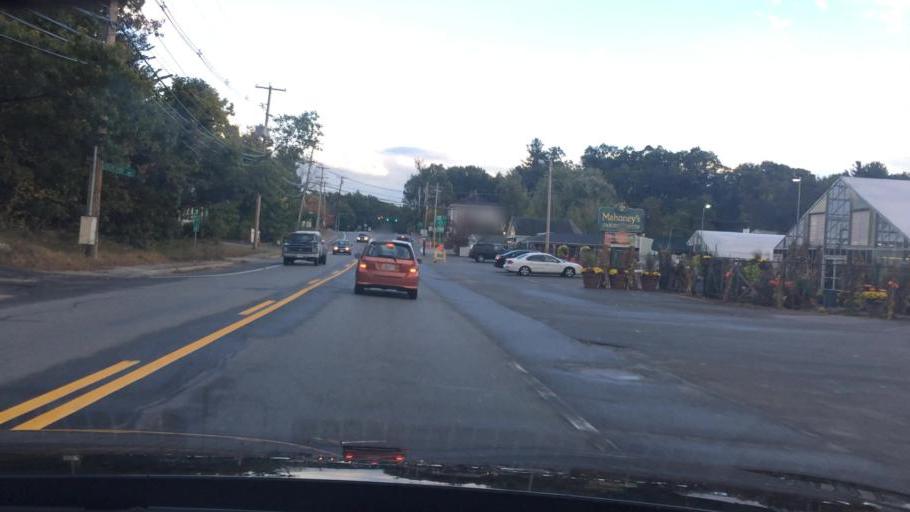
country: US
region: Massachusetts
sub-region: Middlesex County
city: Chelmsford
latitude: 42.6332
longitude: -71.3762
